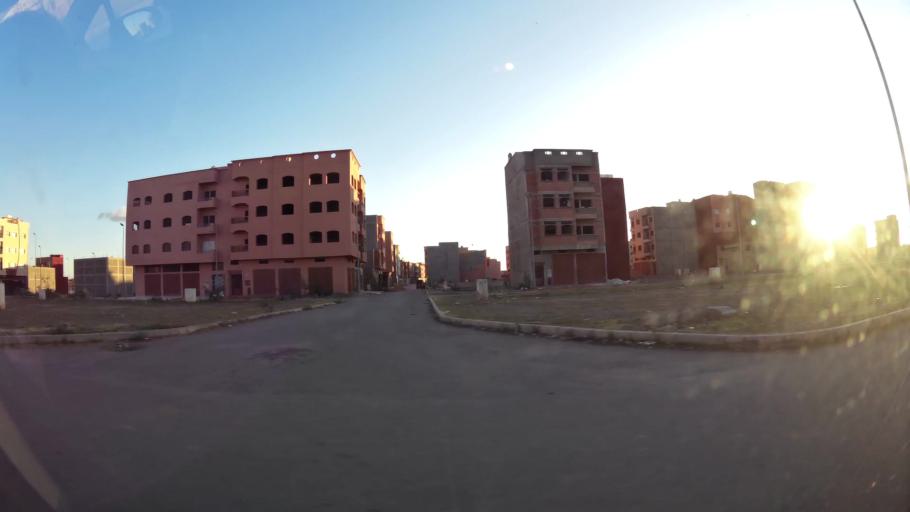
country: MA
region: Marrakech-Tensift-Al Haouz
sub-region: Kelaa-Des-Sraghna
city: Sidi Abdallah
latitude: 32.2382
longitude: -7.9447
